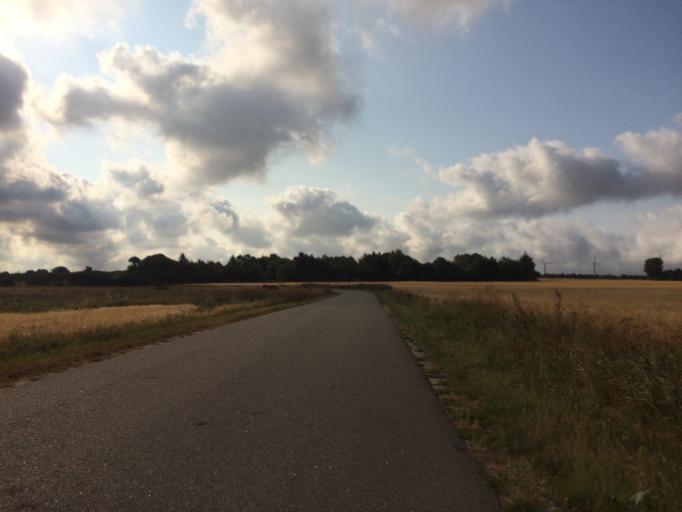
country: DK
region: Central Jutland
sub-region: Holstebro Kommune
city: Vinderup
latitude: 56.6071
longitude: 8.7889
